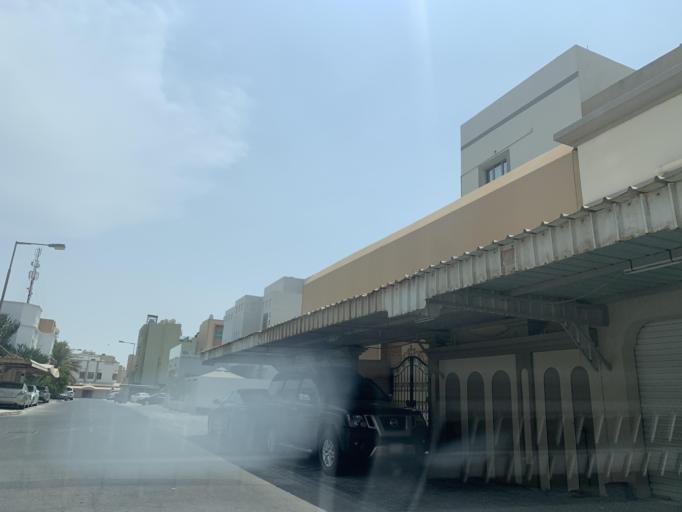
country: BH
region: Muharraq
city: Al Hadd
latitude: 26.2760
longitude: 50.6559
